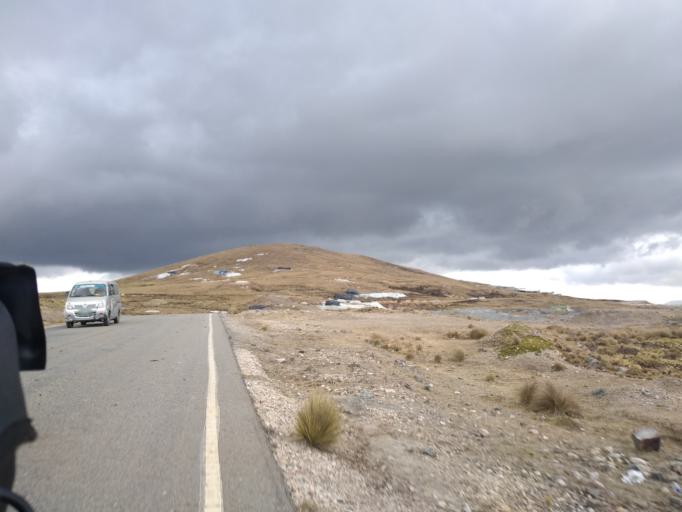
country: PE
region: La Libertad
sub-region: Provincia de Santiago de Chuco
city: Quiruvilca
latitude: -7.9937
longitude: -78.2943
